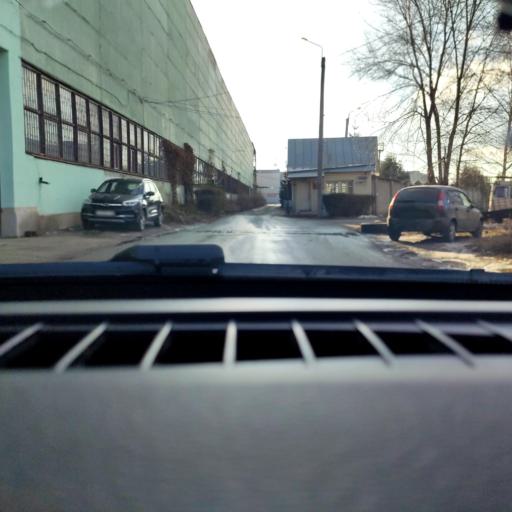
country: RU
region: Voronezj
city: Voronezh
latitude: 51.6642
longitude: 39.1771
